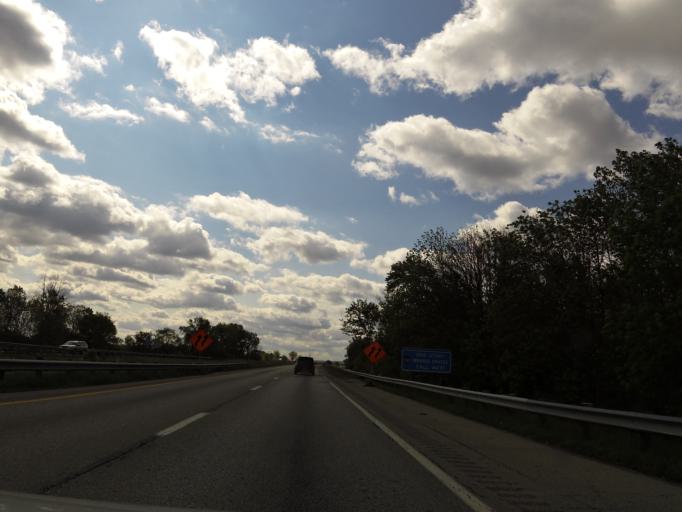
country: US
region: Ohio
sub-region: Franklin County
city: Groveport
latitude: 39.8752
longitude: -82.8615
